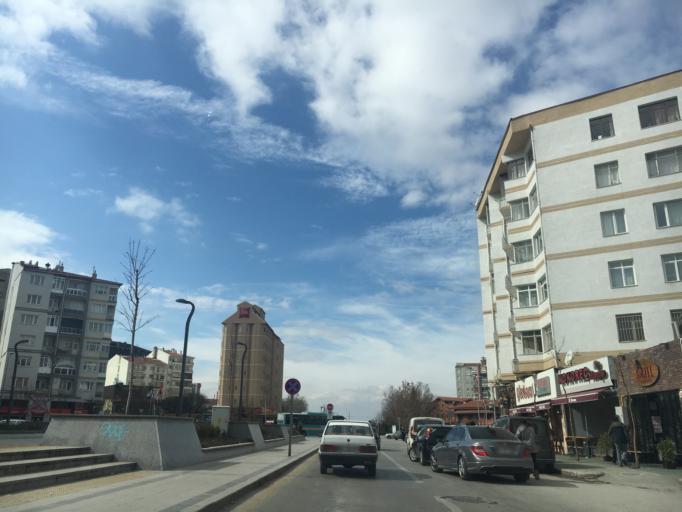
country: TR
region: Eskisehir
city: Eskisehir
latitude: 39.7813
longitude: 30.5150
